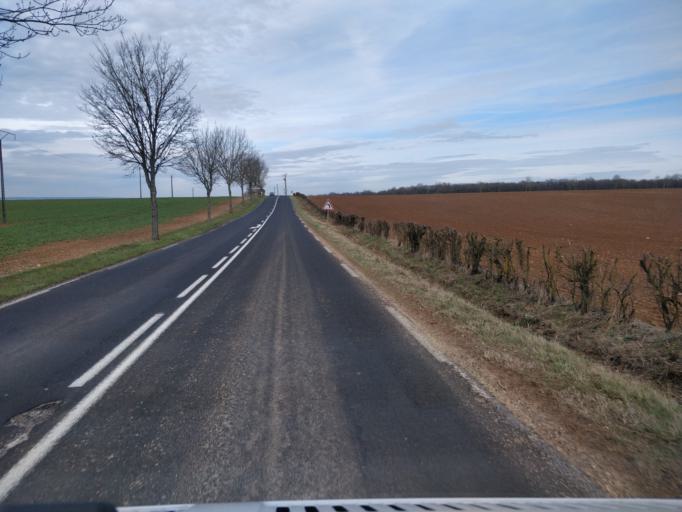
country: FR
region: Lorraine
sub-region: Departement de Meurthe-et-Moselle
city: Montauville
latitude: 48.9279
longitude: 5.9036
